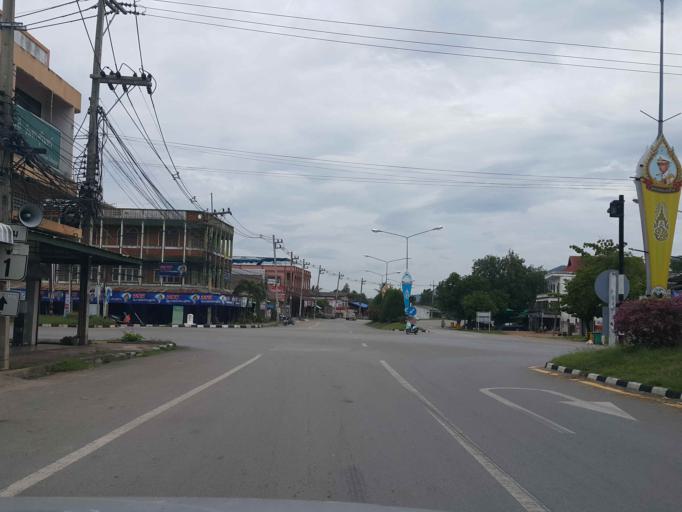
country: TH
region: Lampang
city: Thoen
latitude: 17.6401
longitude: 99.2356
